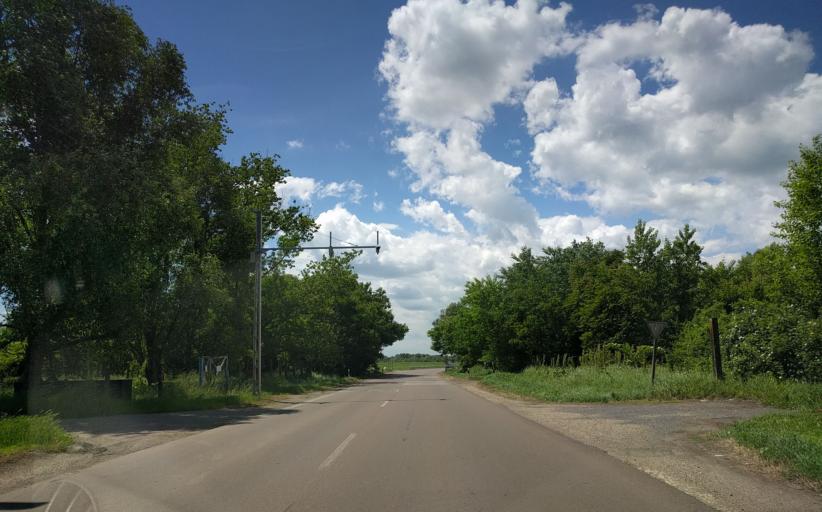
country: HU
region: Jasz-Nagykun-Szolnok
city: Toszeg
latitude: 47.1327
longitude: 20.1446
